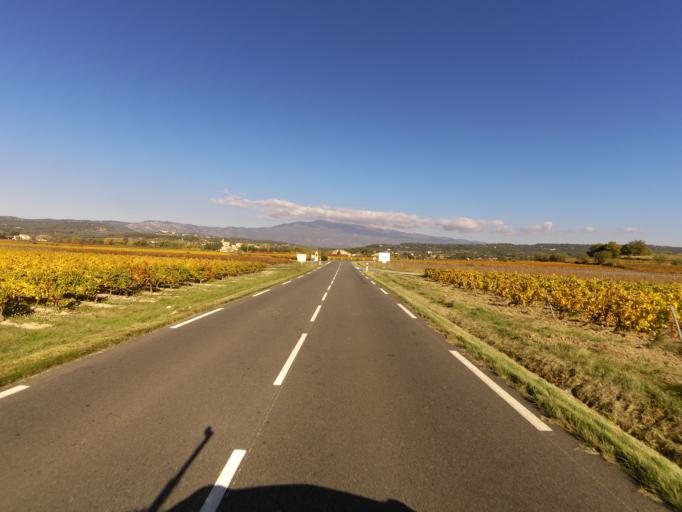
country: FR
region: Provence-Alpes-Cote d'Azur
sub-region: Departement du Vaucluse
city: Caromb
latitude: 44.0918
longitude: 5.1296
